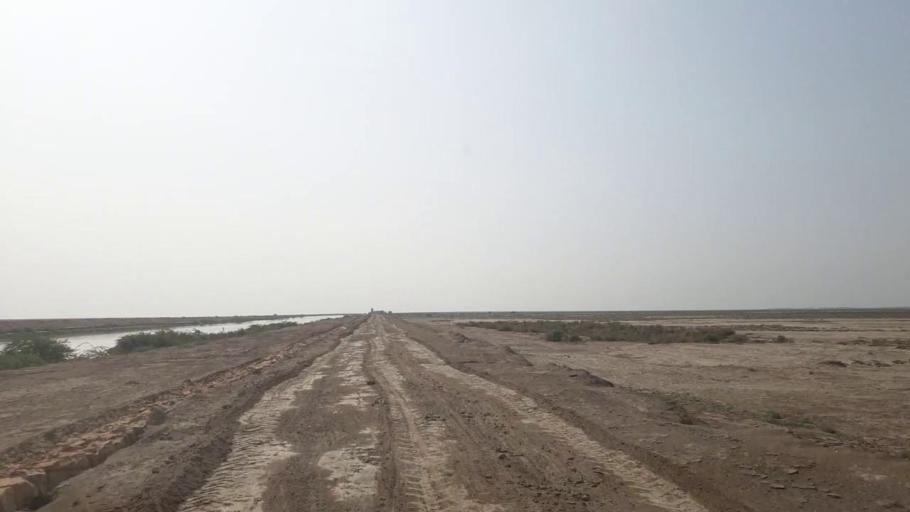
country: PK
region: Sindh
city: Kadhan
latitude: 24.3300
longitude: 68.8332
